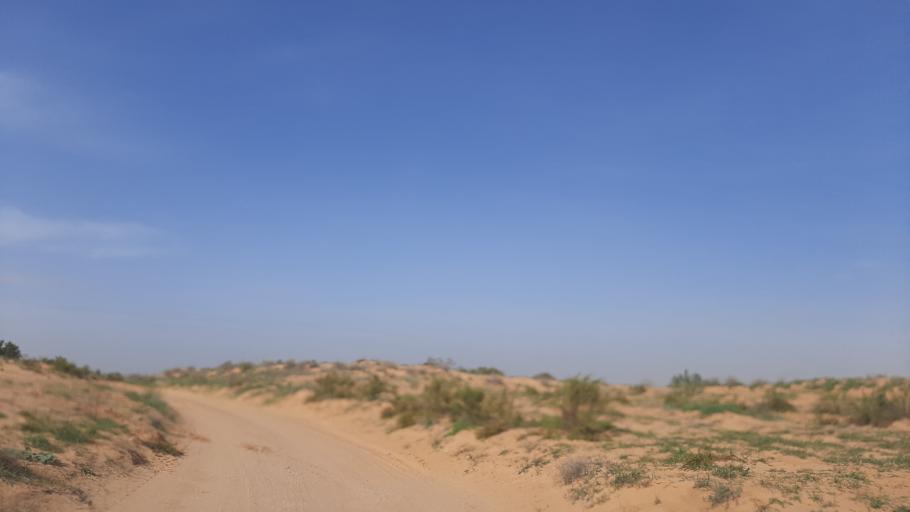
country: TN
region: Madanin
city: Zarzis
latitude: 33.4366
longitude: 10.8080
